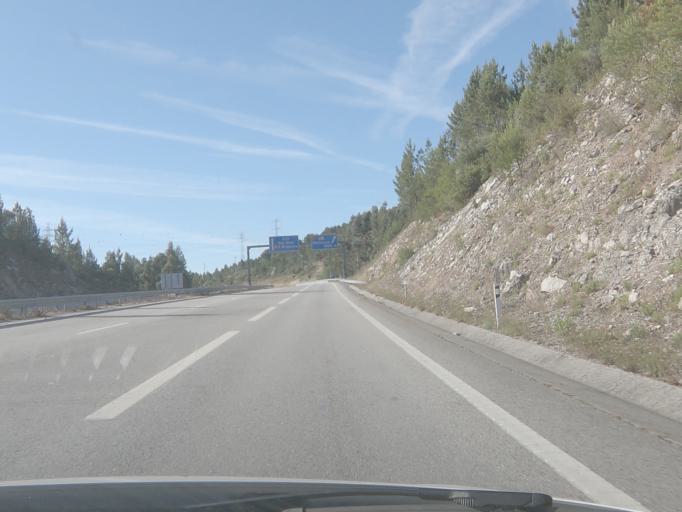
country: PT
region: Viseu
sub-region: Castro Daire
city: Castro Daire
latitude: 40.8123
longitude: -7.9385
